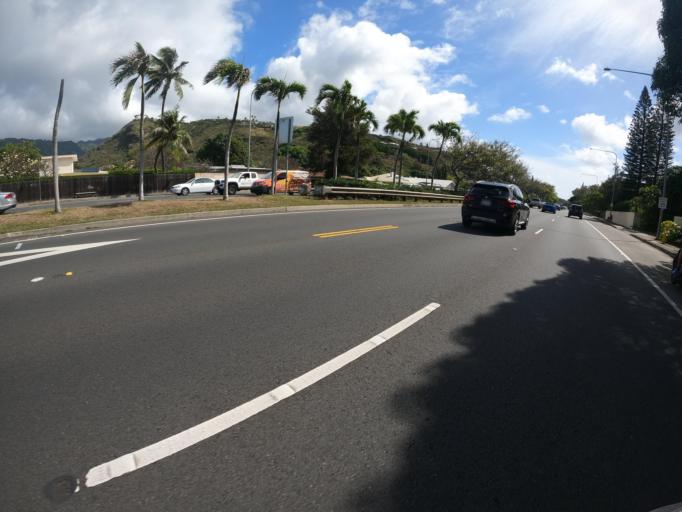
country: US
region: Hawaii
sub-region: Honolulu County
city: Waimanalo
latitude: 21.2785
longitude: -157.7488
